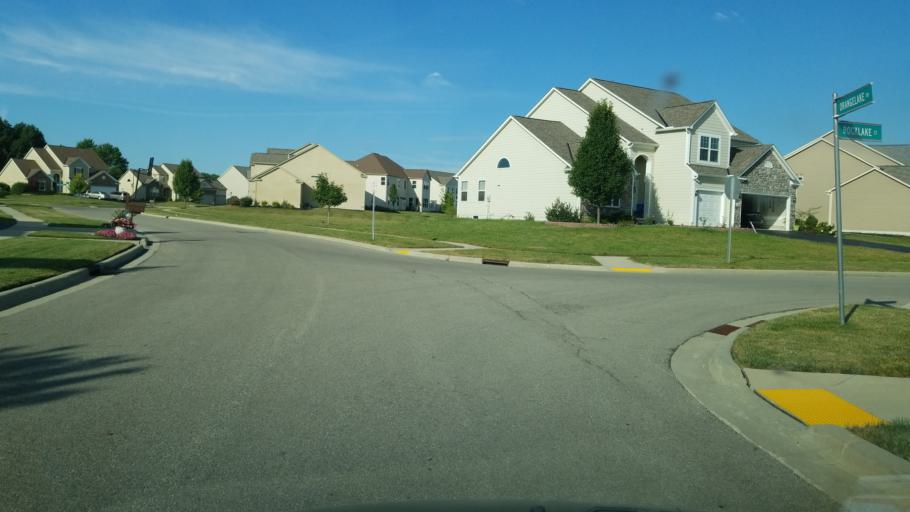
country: US
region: Ohio
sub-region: Delaware County
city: Lewis Center
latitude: 40.1865
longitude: -82.9978
